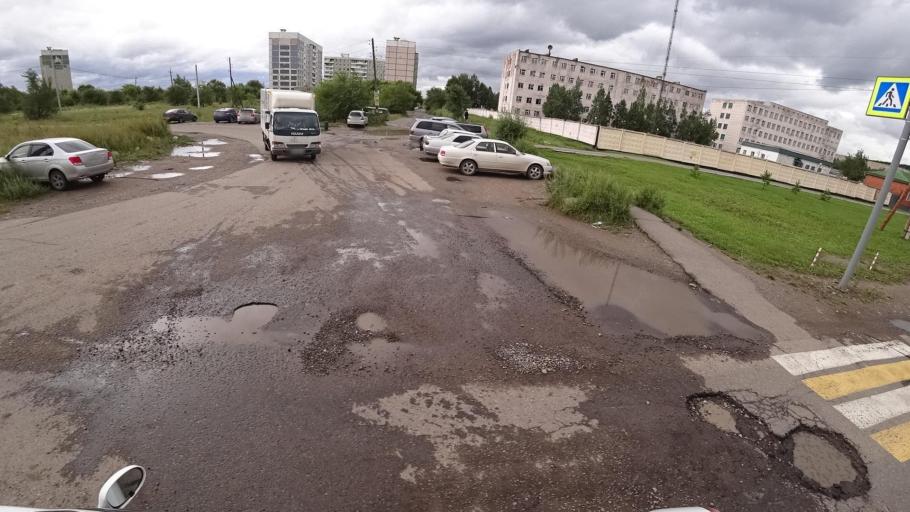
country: RU
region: Khabarovsk Krai
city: Solnechnyy
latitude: 50.5947
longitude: 137.0378
